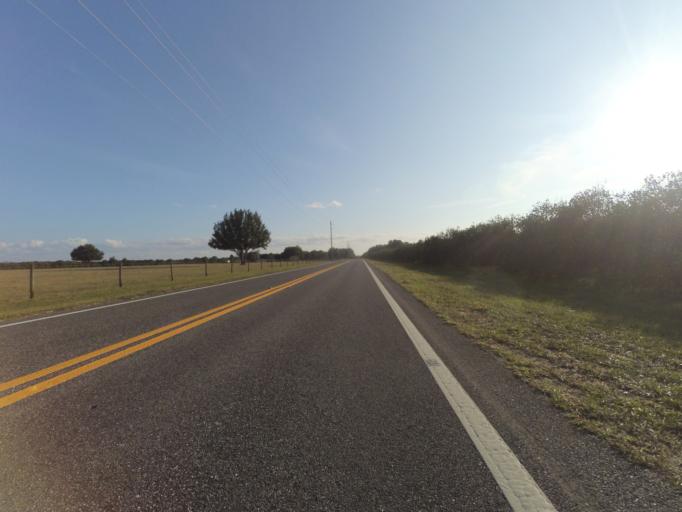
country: US
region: Florida
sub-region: Lake County
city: Umatilla
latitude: 28.9529
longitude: -81.6789
